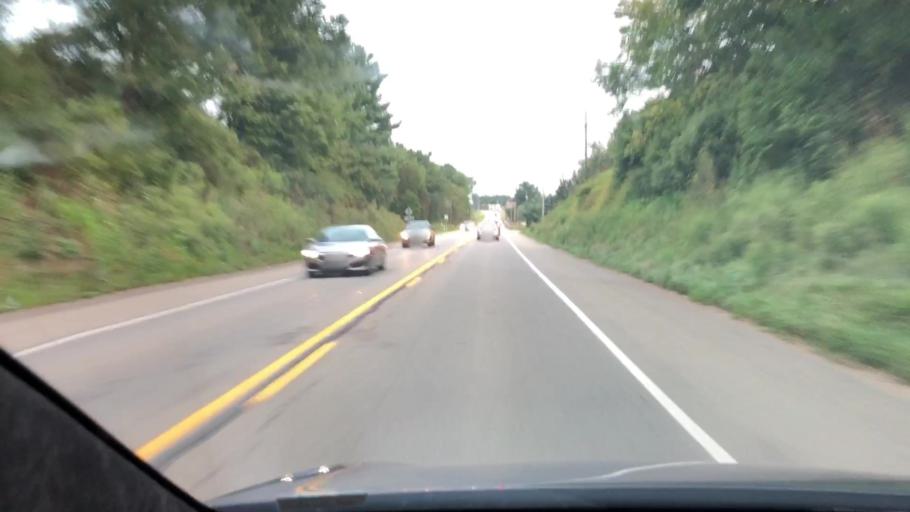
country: US
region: Pennsylvania
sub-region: Butler County
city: Shanor-Northvue
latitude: 40.9274
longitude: -79.9515
